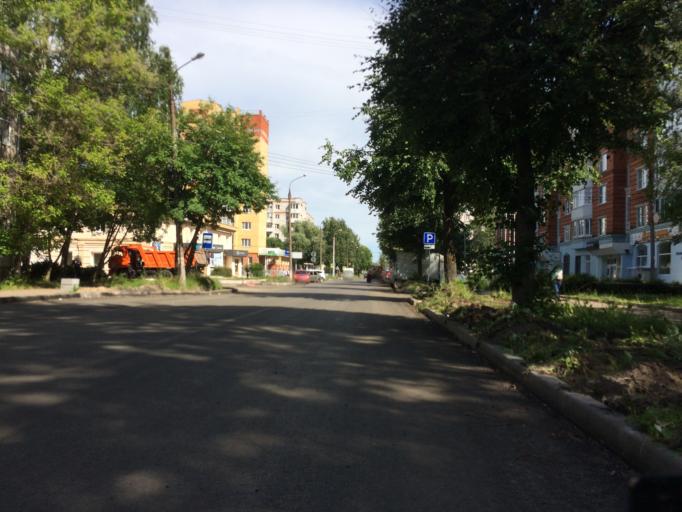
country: RU
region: Mariy-El
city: Yoshkar-Ola
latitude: 56.6448
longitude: 47.8965
